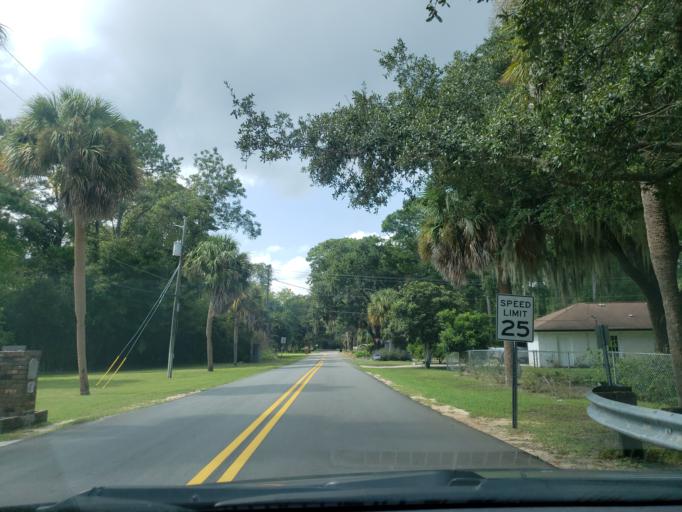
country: US
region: Georgia
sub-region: Chatham County
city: Montgomery
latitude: 31.9305
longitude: -81.0927
